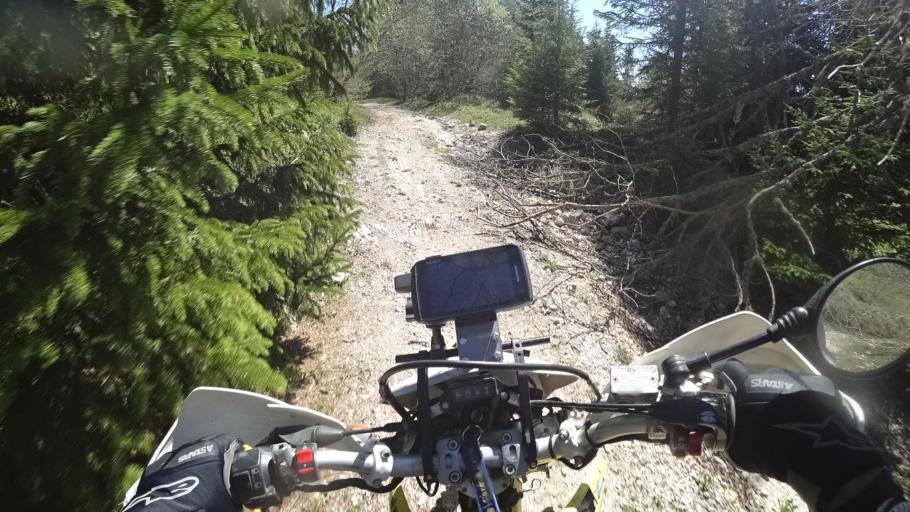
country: BA
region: Federation of Bosnia and Herzegovina
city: Rumboci
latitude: 43.8644
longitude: 17.4785
